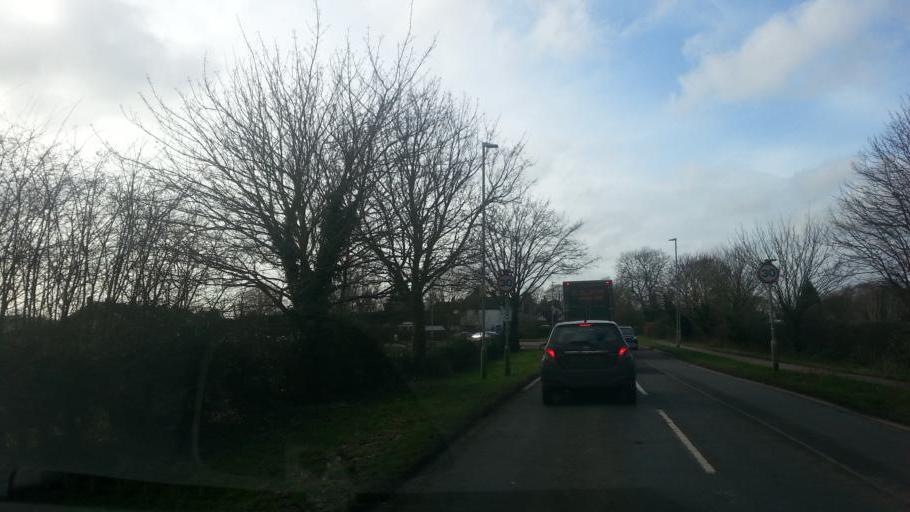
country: GB
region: England
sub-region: District of Rutland
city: Manton
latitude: 52.6320
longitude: -0.6947
